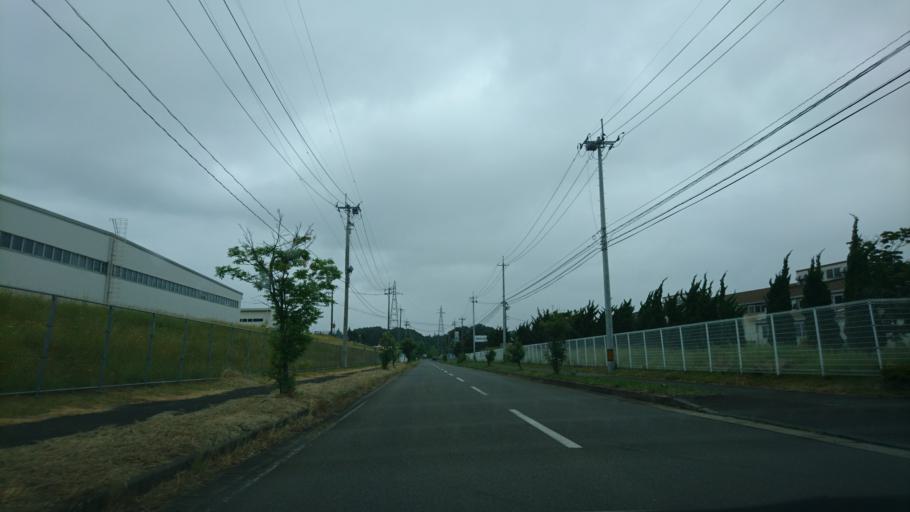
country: JP
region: Iwate
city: Ichinoseki
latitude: 38.9227
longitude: 141.1643
